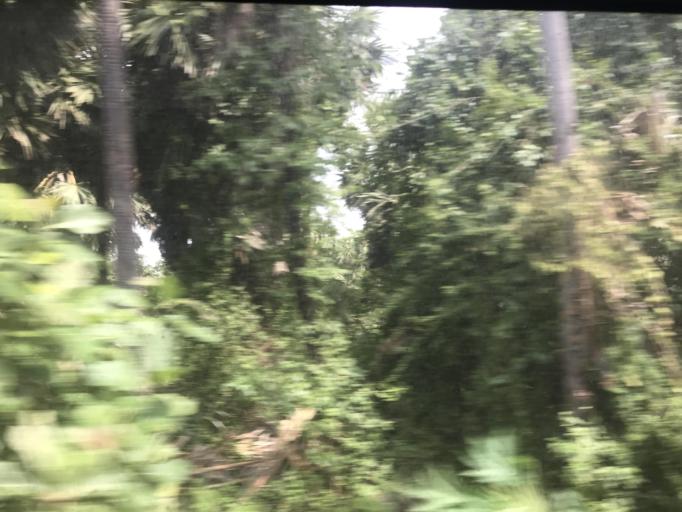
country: LK
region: Northern Province
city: Kilinochchi
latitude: 9.5775
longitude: 80.3559
